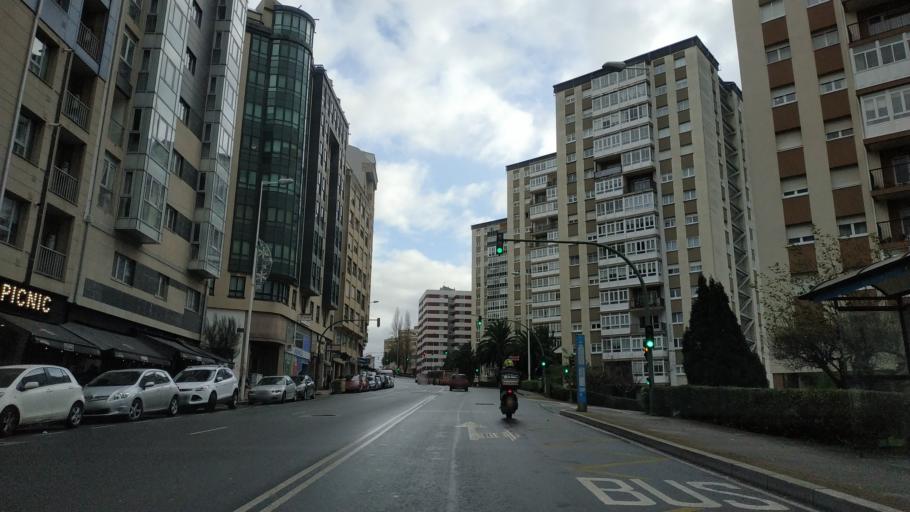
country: ES
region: Galicia
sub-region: Provincia da Coruna
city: A Coruna
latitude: 43.3488
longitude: -8.4032
